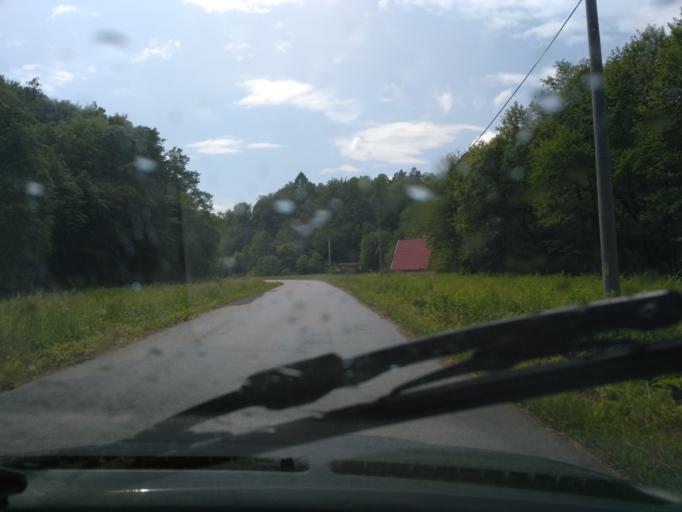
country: PL
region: Subcarpathian Voivodeship
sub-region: Powiat przeworski
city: Jawornik Polski
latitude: 49.9313
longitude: 22.2788
